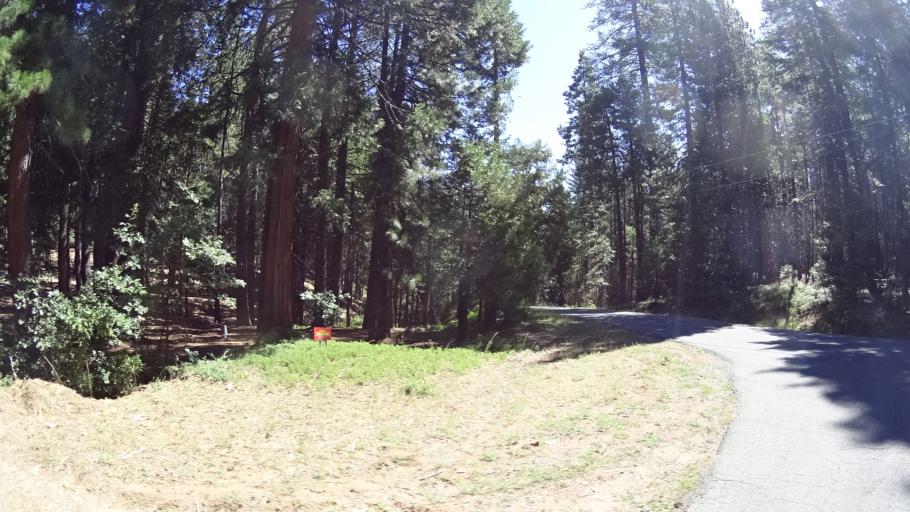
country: US
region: California
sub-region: Calaveras County
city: Arnold
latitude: 38.2850
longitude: -120.2767
